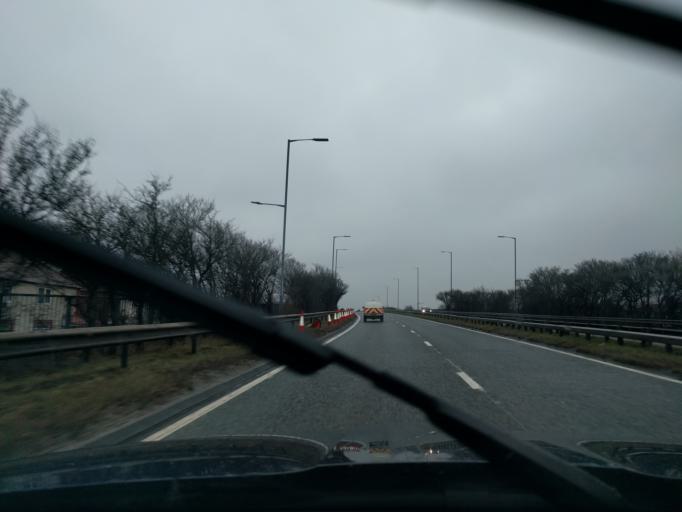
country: GB
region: England
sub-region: South Tyneside
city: Jarrow
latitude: 54.9673
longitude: -1.4744
